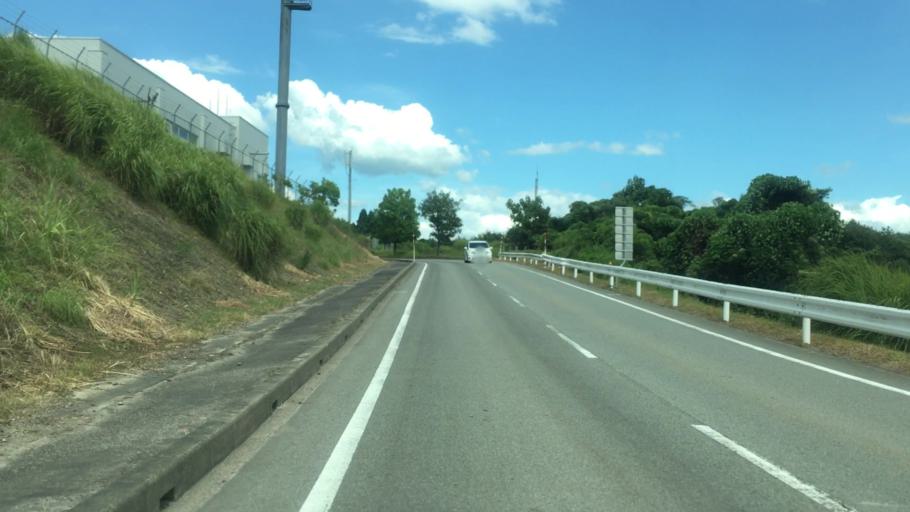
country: JP
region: Hyogo
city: Toyooka
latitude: 35.5153
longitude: 134.7887
